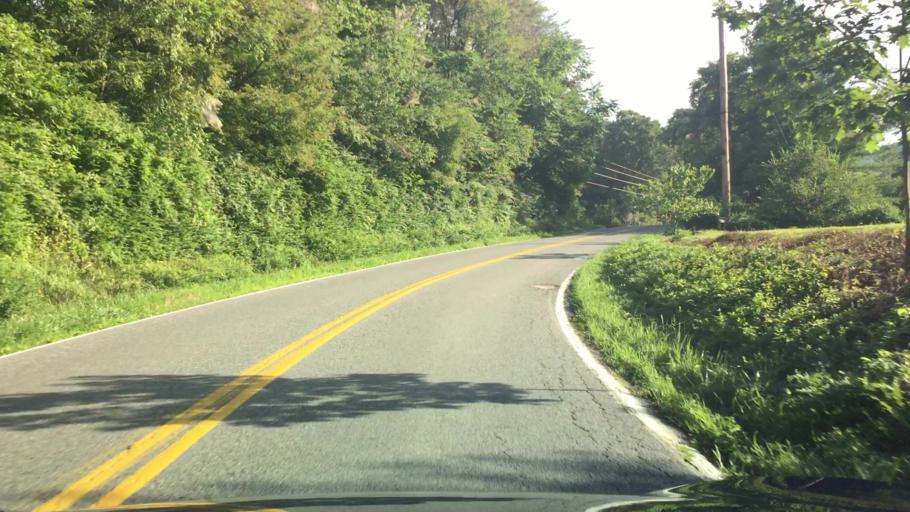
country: US
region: Virginia
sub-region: Wythe County
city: Wytheville
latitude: 36.9406
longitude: -80.9720
